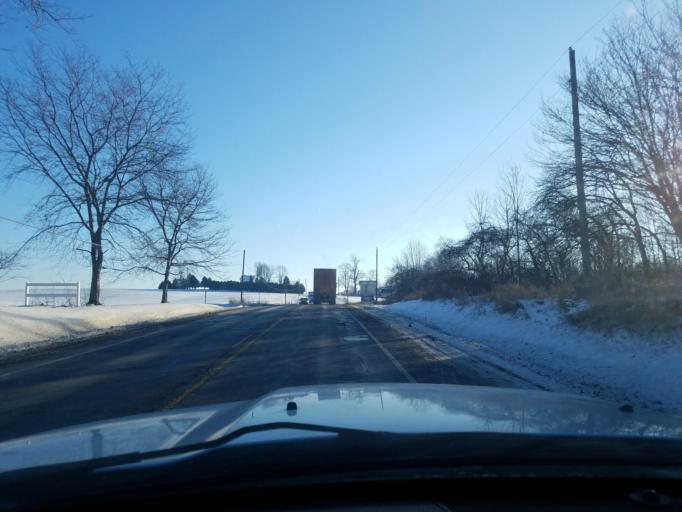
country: US
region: Indiana
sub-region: Noble County
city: Rome City
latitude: 41.4528
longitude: -85.3582
